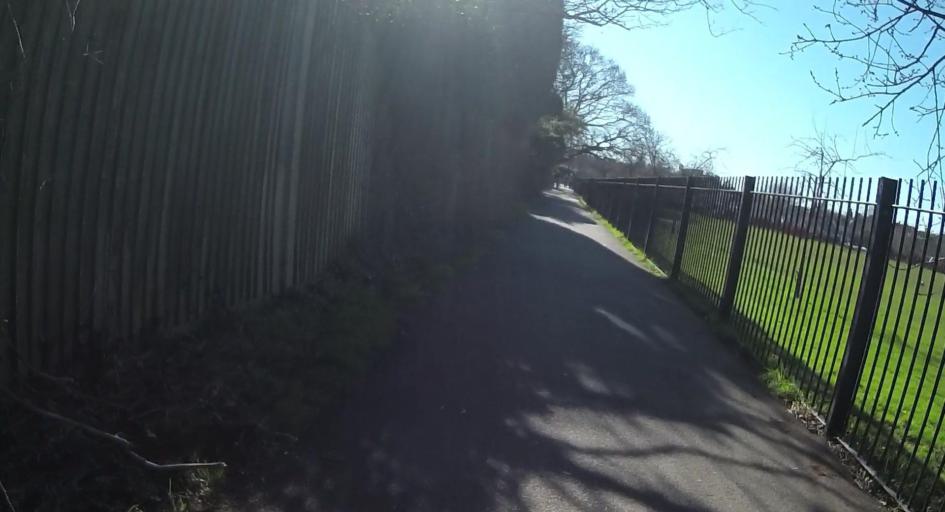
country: GB
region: England
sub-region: Surrey
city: Weybridge
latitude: 51.3706
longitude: -0.4566
